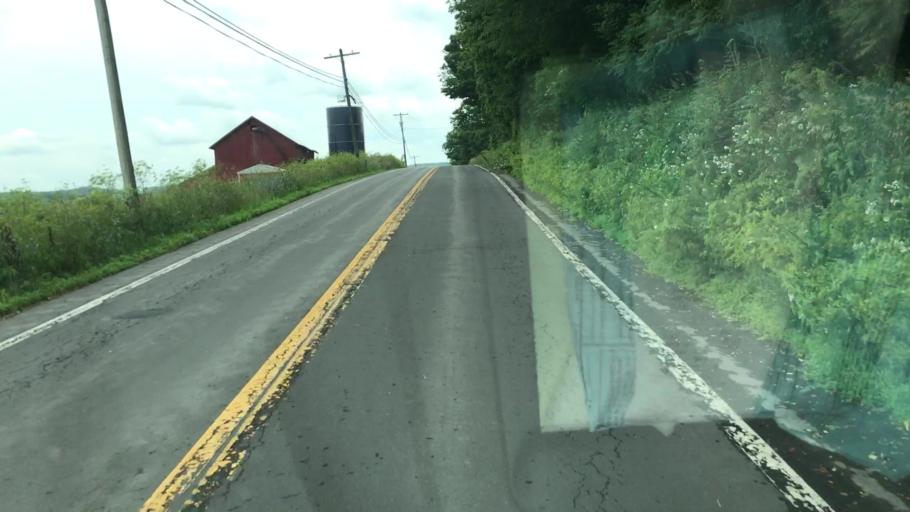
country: US
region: New York
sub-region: Onondaga County
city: Manlius
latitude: 42.9614
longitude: -75.9867
